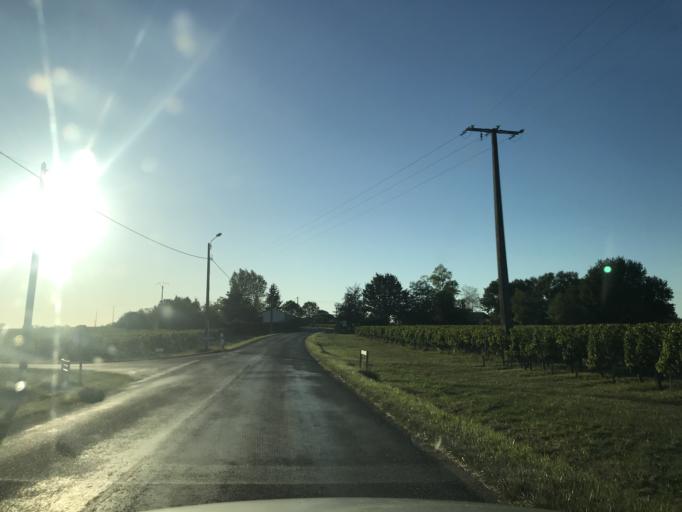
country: FR
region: Aquitaine
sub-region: Departement de la Gironde
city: Mouliets-et-Villemartin
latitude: 44.8945
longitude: -0.0538
